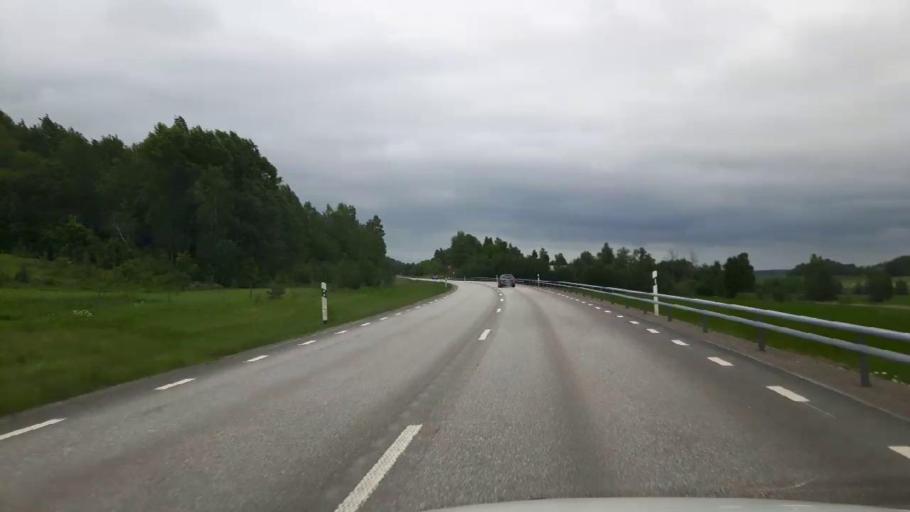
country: SE
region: Vaestmanland
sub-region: Kopings Kommun
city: Kolsva
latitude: 59.5690
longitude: 15.8802
